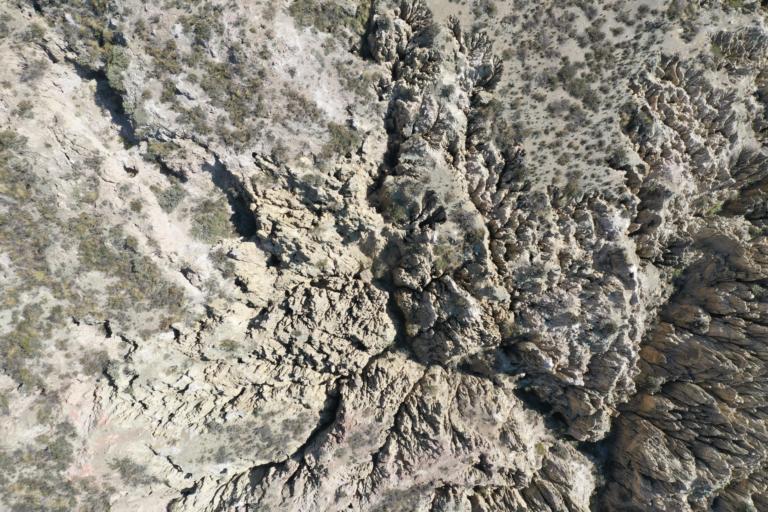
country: BO
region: La Paz
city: La Paz
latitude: -16.5624
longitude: -68.1299
